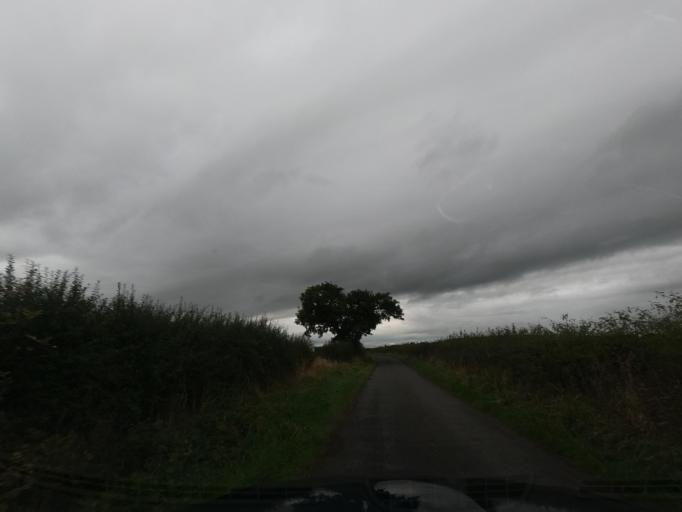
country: GB
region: England
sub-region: Northumberland
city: Ford
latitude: 55.6162
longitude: -2.0742
